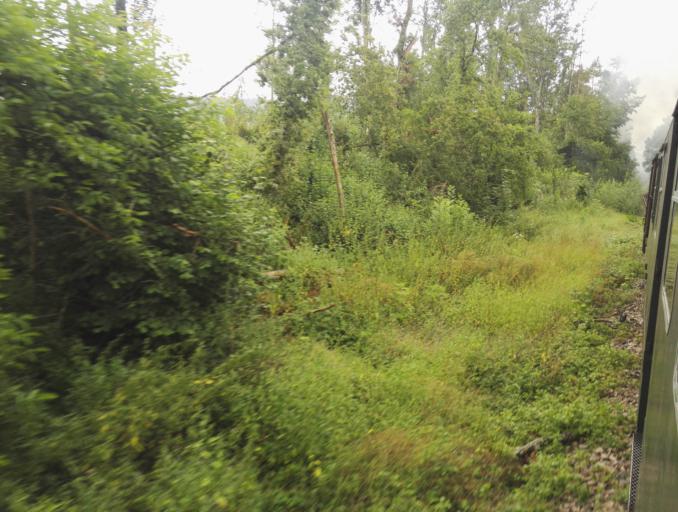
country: DE
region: Baden-Wuerttemberg
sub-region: Freiburg Region
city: Blumberg
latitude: 47.7937
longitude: 8.5169
